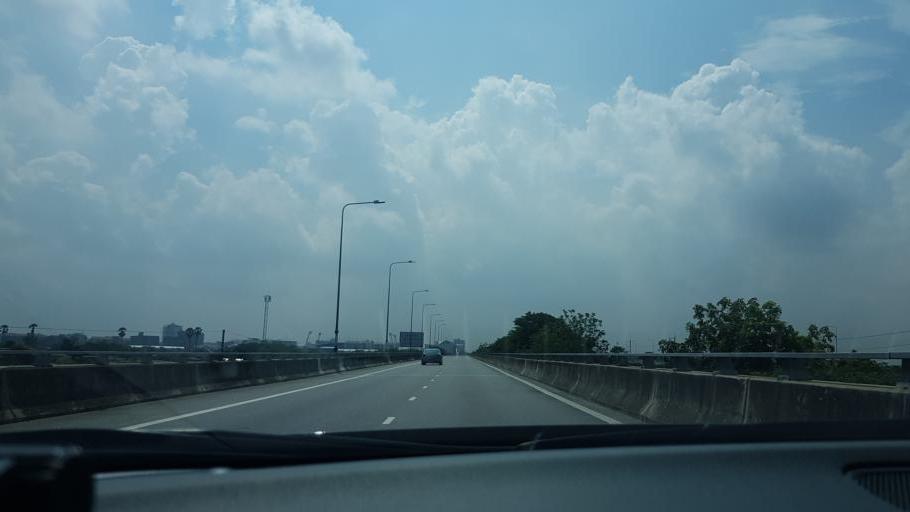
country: TH
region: Pathum Thani
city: Khlong Luang
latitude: 14.0663
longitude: 100.5848
